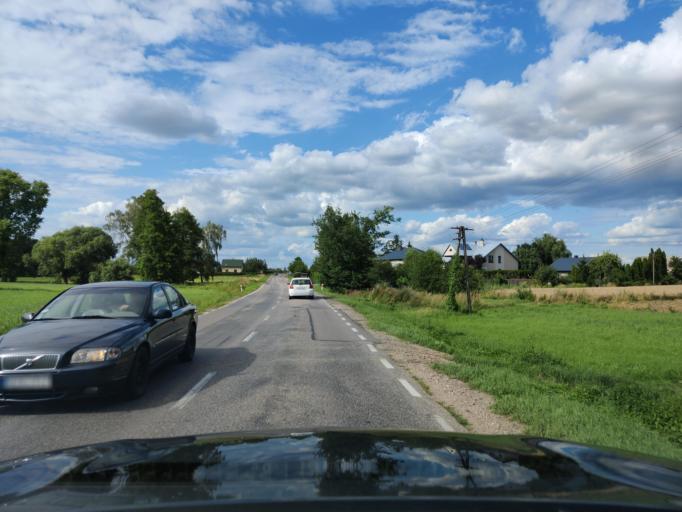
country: PL
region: Podlasie
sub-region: Powiat zambrowski
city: Zambrow
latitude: 52.8995
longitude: 22.2530
